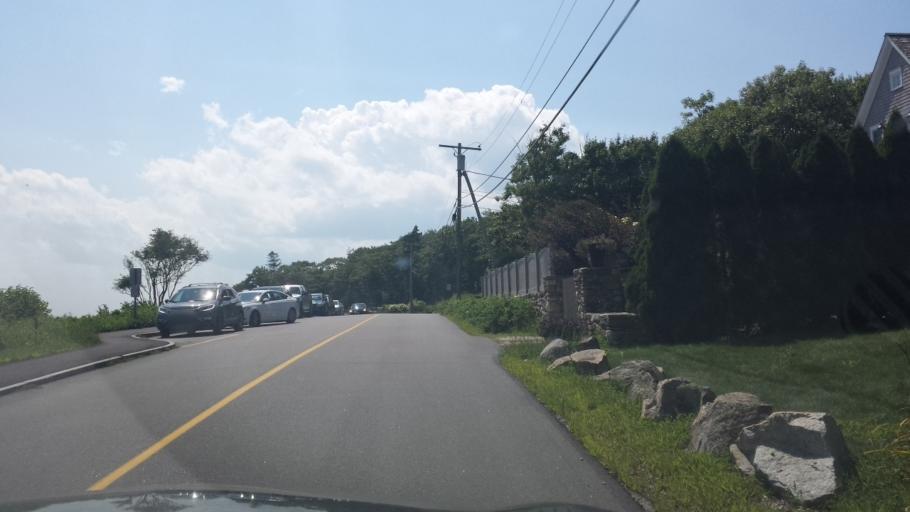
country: US
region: Maine
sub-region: York County
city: Kennebunkport
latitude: 43.3447
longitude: -70.4625
